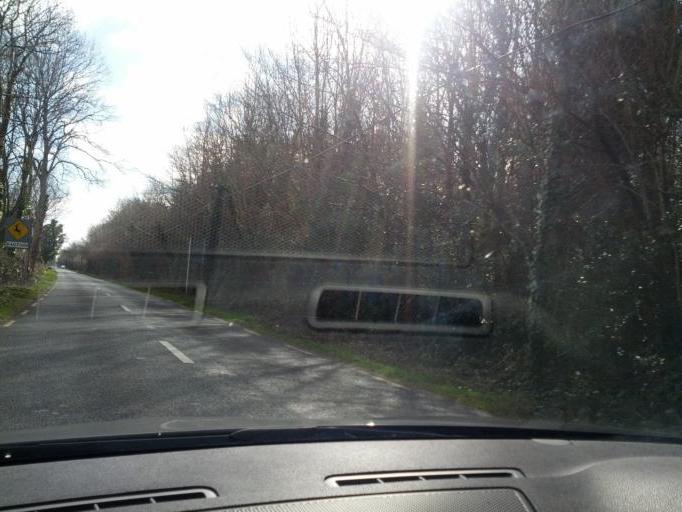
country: IE
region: Connaught
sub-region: County Galway
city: Ballinasloe
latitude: 53.4176
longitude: -8.3763
